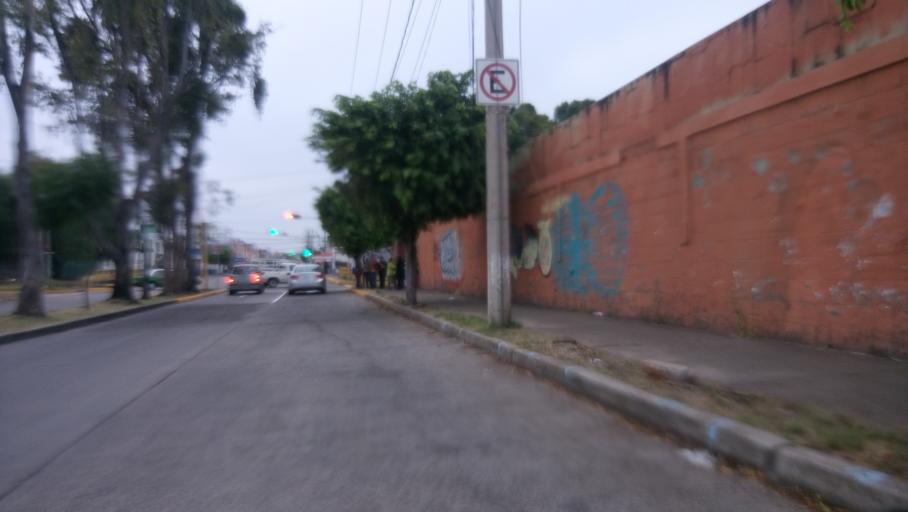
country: MX
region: Guanajuato
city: Leon
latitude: 21.1420
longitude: -101.6650
